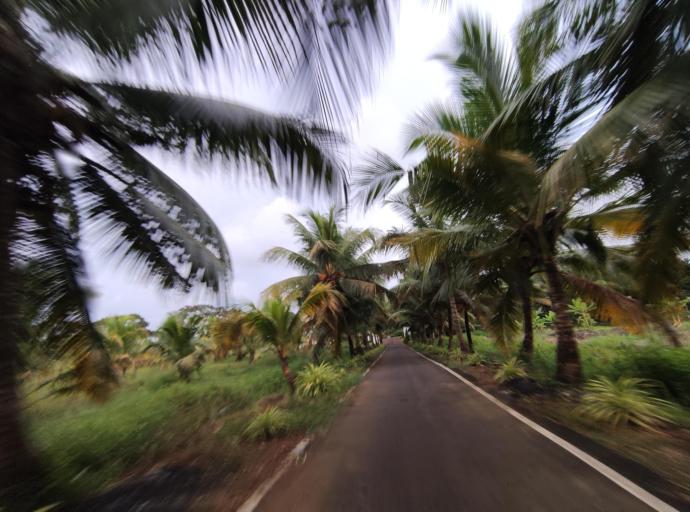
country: IN
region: Kerala
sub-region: Alappuzha
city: Shertallai
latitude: 9.6398
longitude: 76.4294
